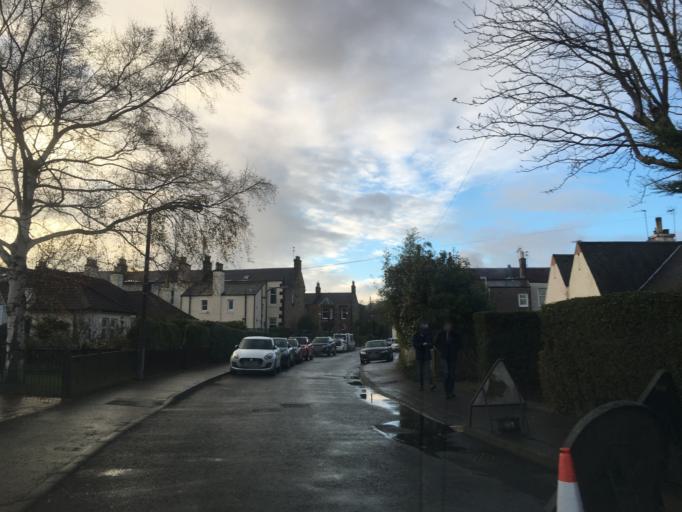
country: GB
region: Scotland
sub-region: Edinburgh
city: Colinton
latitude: 55.9438
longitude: -3.2497
